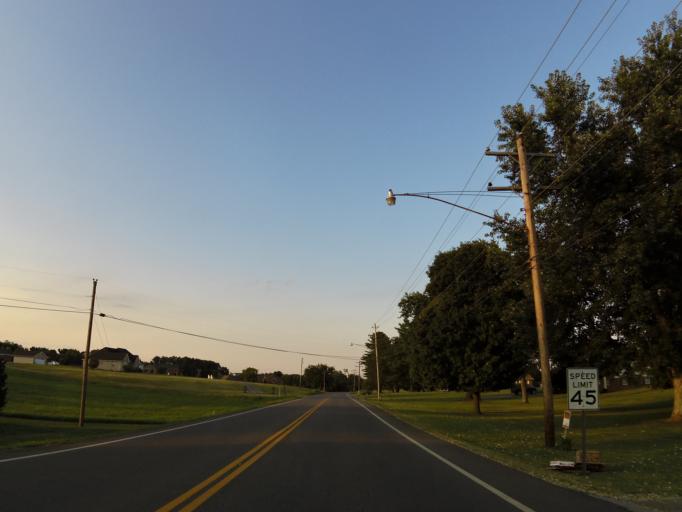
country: US
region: Tennessee
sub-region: Monroe County
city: Sweetwater
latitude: 35.6209
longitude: -84.4548
